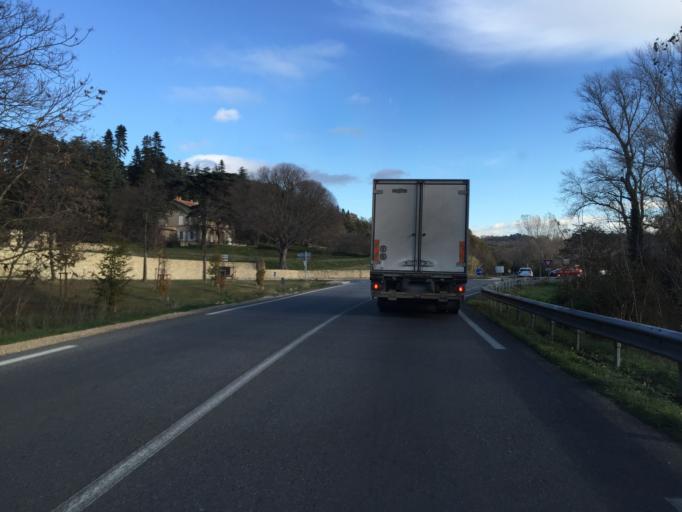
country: FR
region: Provence-Alpes-Cote d'Azur
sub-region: Departement du Vaucluse
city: Goult
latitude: 43.8583
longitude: 5.2362
